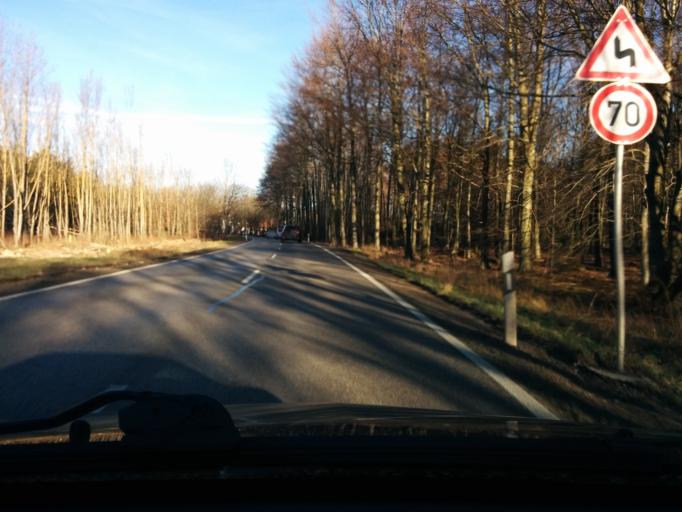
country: DE
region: Bavaria
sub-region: Upper Bavaria
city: Starnberg
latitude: 48.0286
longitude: 11.3059
